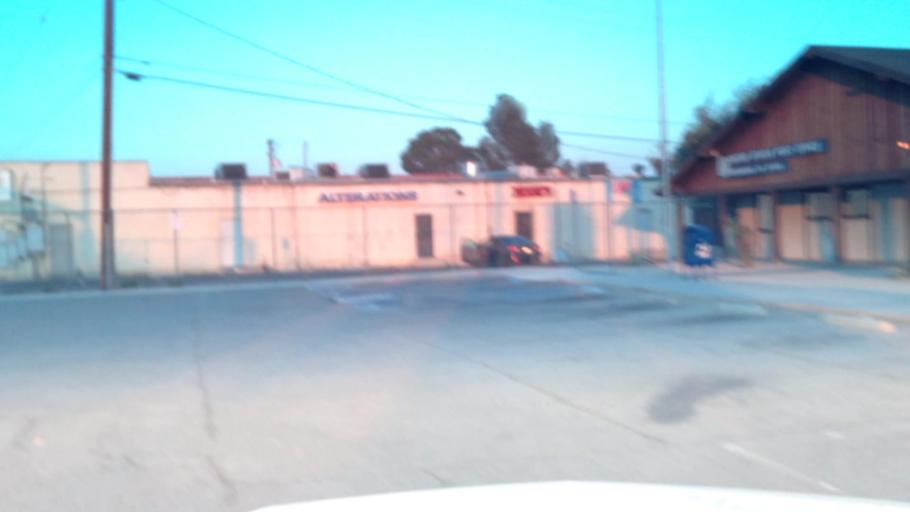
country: US
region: California
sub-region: Kern County
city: Rosamond
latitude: 34.8641
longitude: -118.1670
